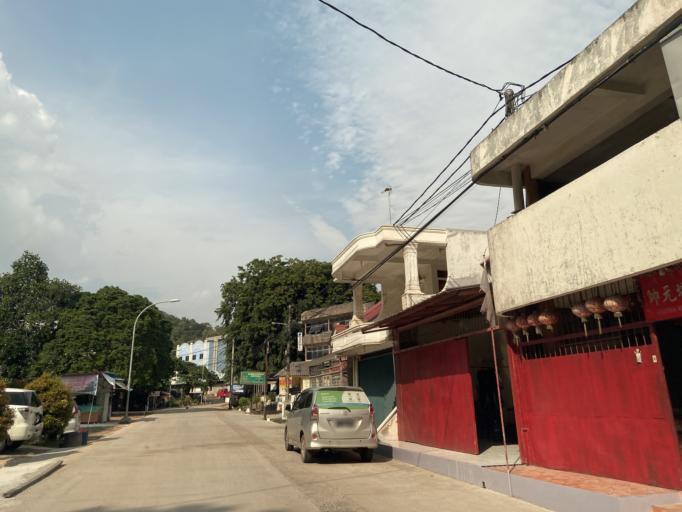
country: SG
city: Singapore
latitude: 1.1245
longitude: 104.0149
